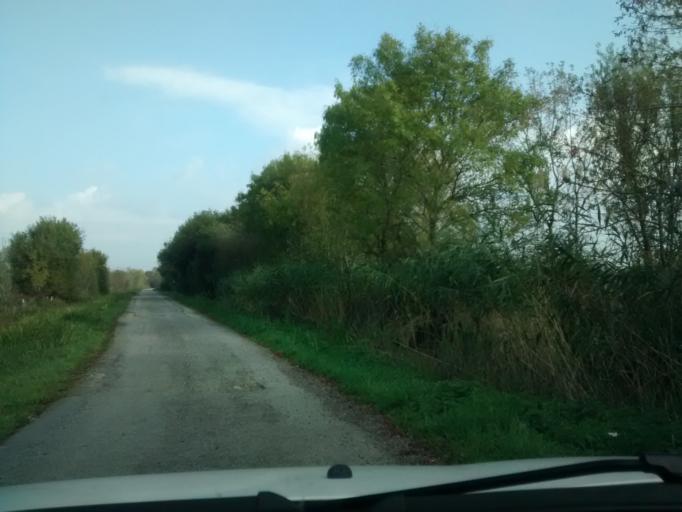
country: FR
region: Pays de la Loire
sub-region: Departement de la Loire-Atlantique
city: Cordemais
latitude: 47.2479
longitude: -1.8634
